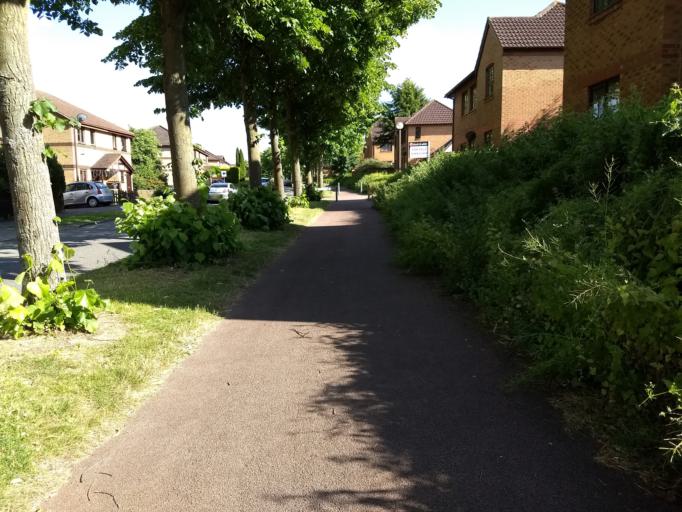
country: GB
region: England
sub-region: Milton Keynes
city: Shenley Church End
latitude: 52.0240
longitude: -0.7843
